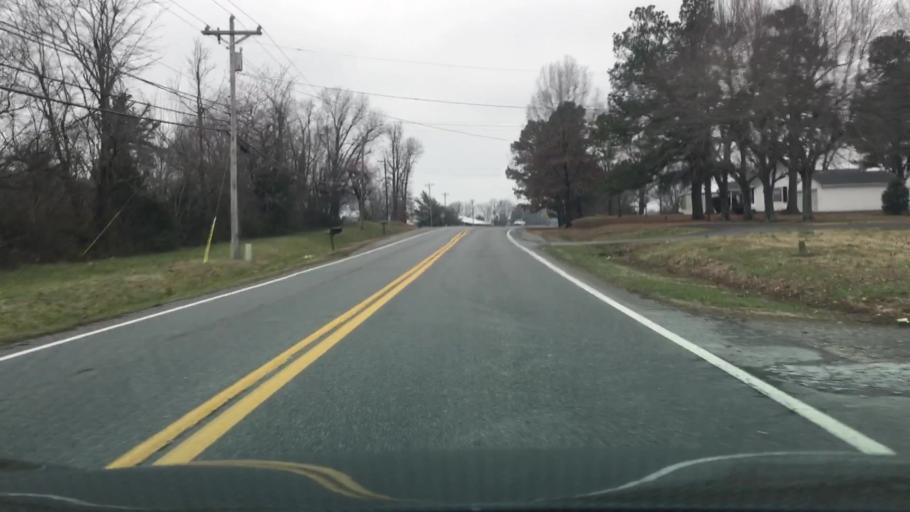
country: US
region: Kentucky
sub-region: McCracken County
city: Reidland
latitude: 36.9872
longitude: -88.5015
